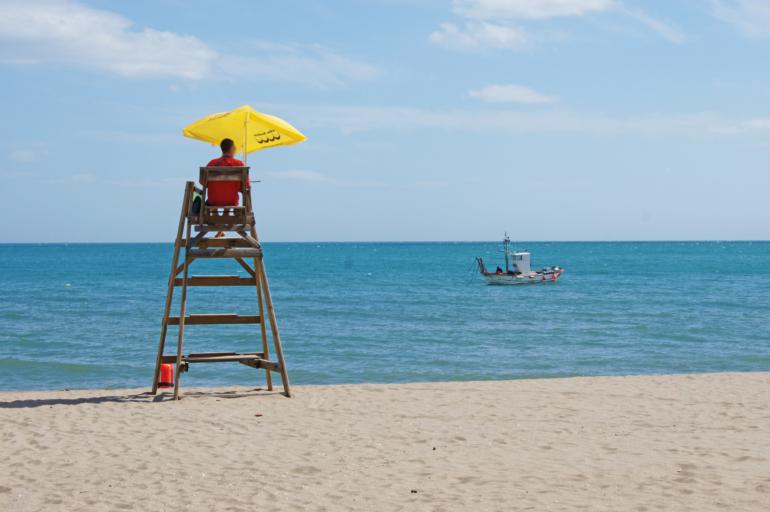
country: ES
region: Andalusia
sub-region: Provincia de Malaga
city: Fuengirola
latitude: 36.5604
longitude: -4.6068
